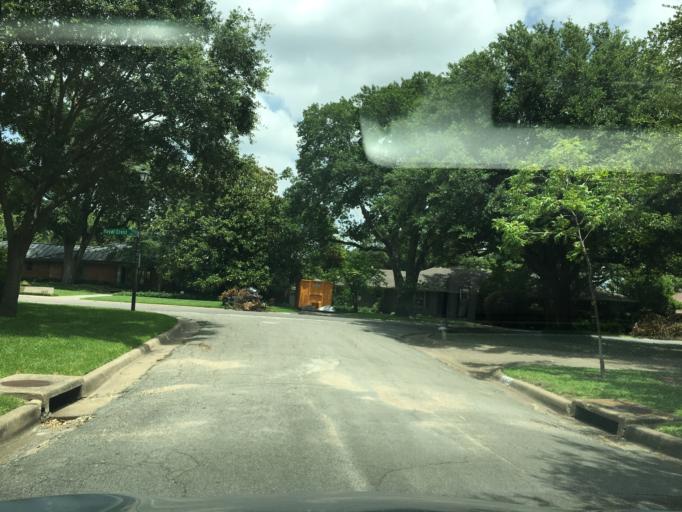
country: US
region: Texas
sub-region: Dallas County
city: University Park
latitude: 32.8998
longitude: -96.7916
